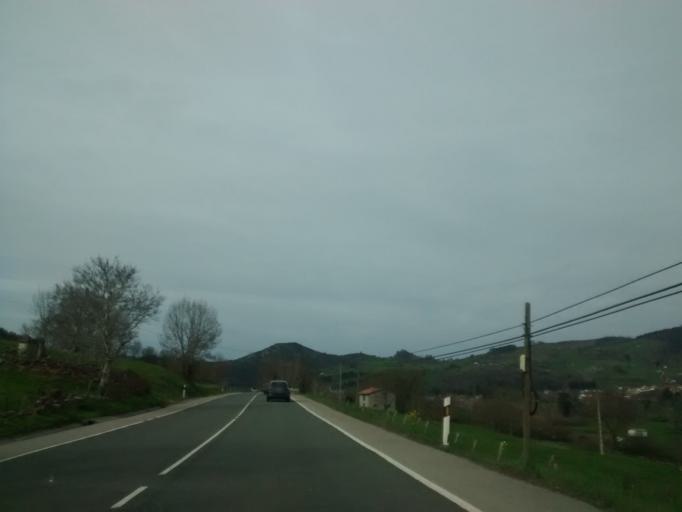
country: ES
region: Cantabria
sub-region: Provincia de Cantabria
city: Corvera
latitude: 43.2590
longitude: -3.9479
